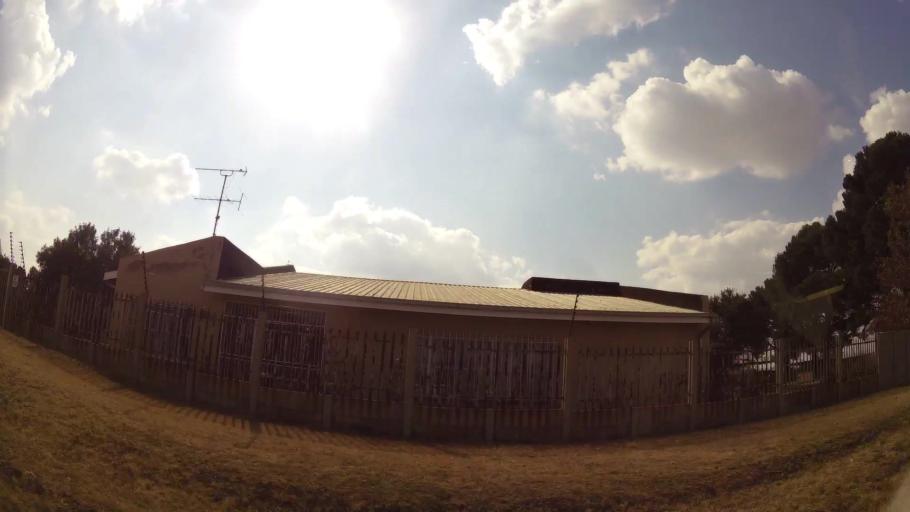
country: ZA
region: Mpumalanga
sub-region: Nkangala District Municipality
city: Delmas
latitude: -26.1604
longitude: 28.5521
